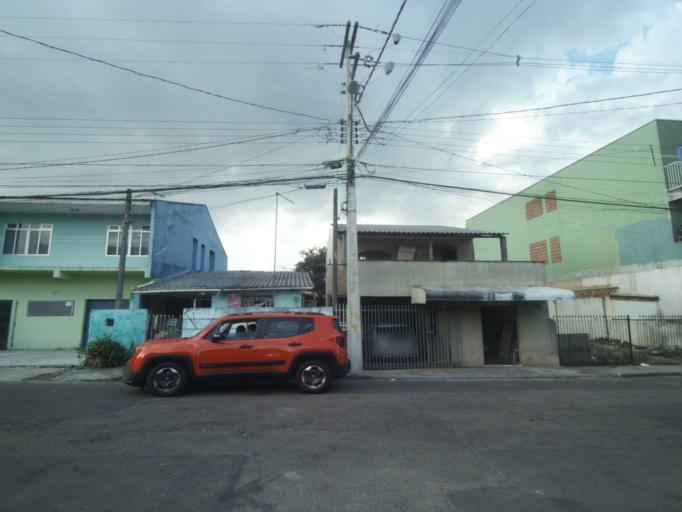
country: BR
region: Parana
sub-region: Sao Jose Dos Pinhais
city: Sao Jose dos Pinhais
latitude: -25.5330
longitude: -49.2752
